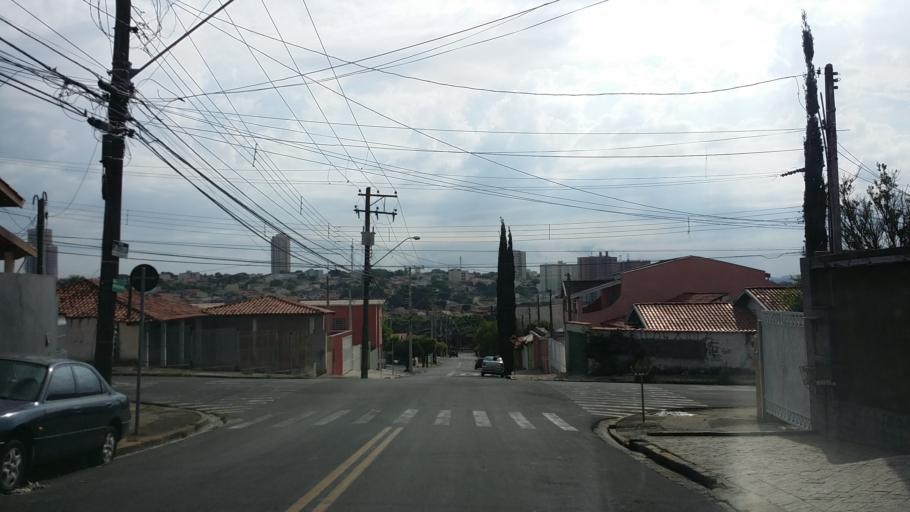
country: BR
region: Sao Paulo
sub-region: Indaiatuba
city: Indaiatuba
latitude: -23.0995
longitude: -47.2065
